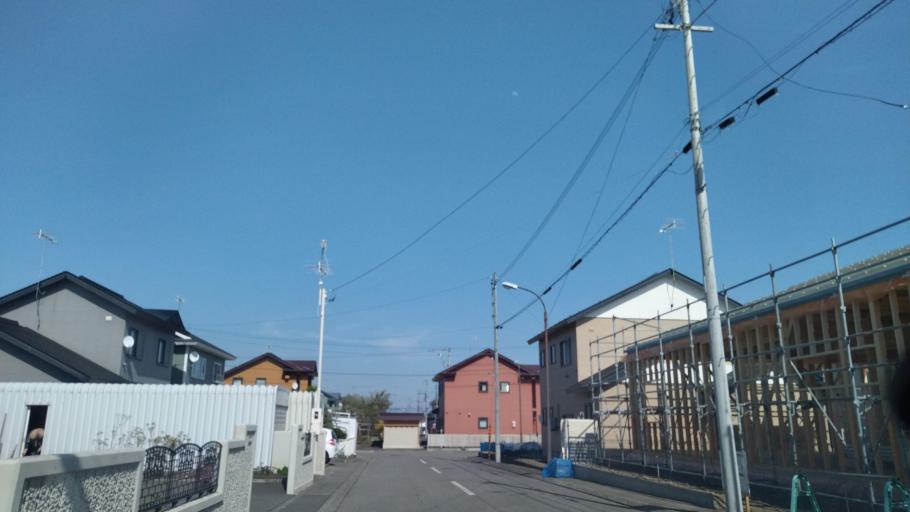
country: JP
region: Hokkaido
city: Obihiro
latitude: 42.9181
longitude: 143.0561
